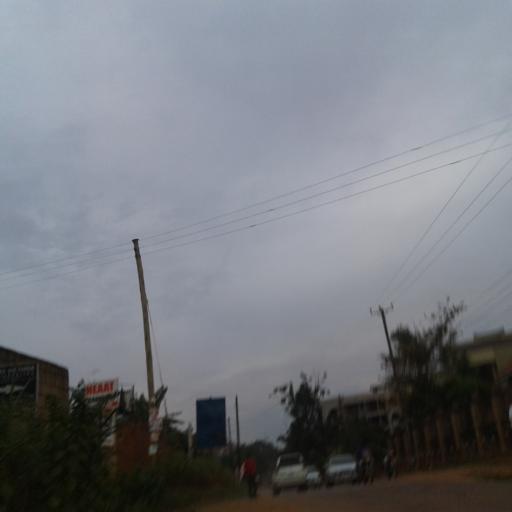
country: UG
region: Central Region
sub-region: Kampala District
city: Kampala
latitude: 0.2505
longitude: 32.6214
